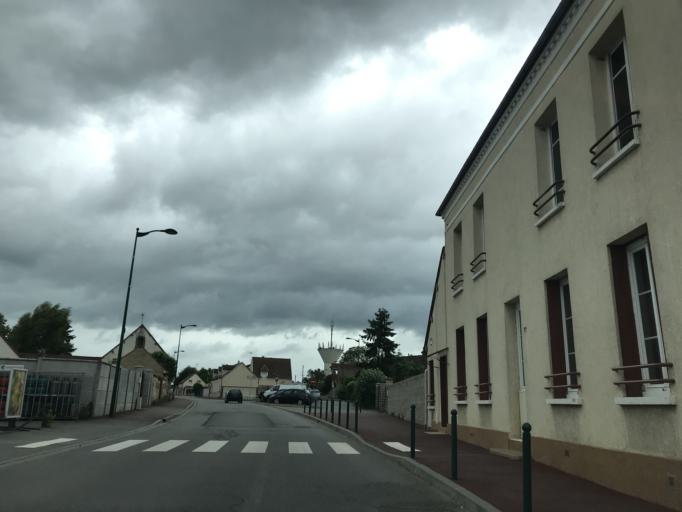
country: FR
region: Haute-Normandie
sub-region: Departement de l'Eure
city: La Couture-Boussey
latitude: 48.8989
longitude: 1.4049
